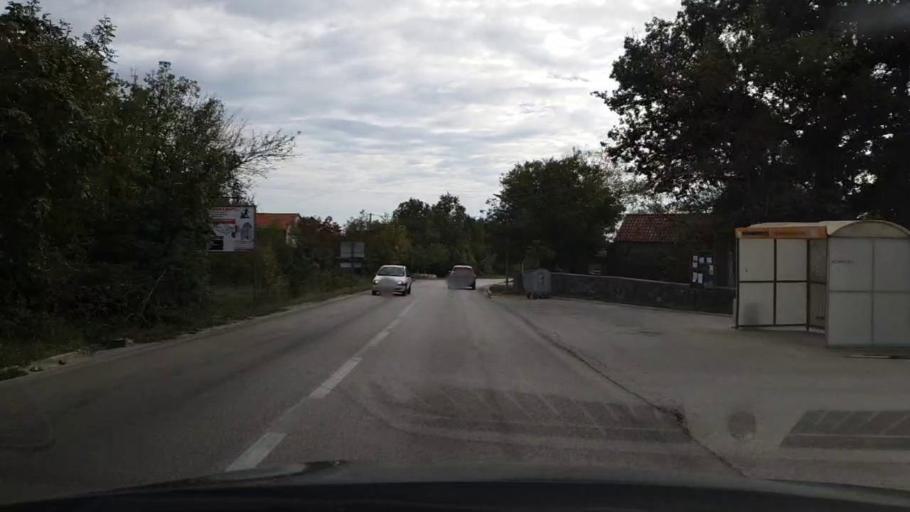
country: ME
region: Herceg Novi
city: Herceg-Novi
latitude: 42.4797
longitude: 18.5293
